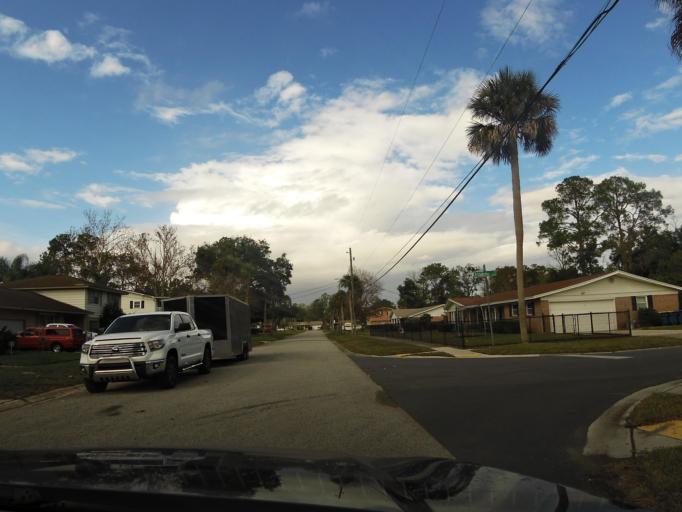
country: US
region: Florida
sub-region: Duval County
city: Jacksonville
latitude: 30.3425
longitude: -81.5656
